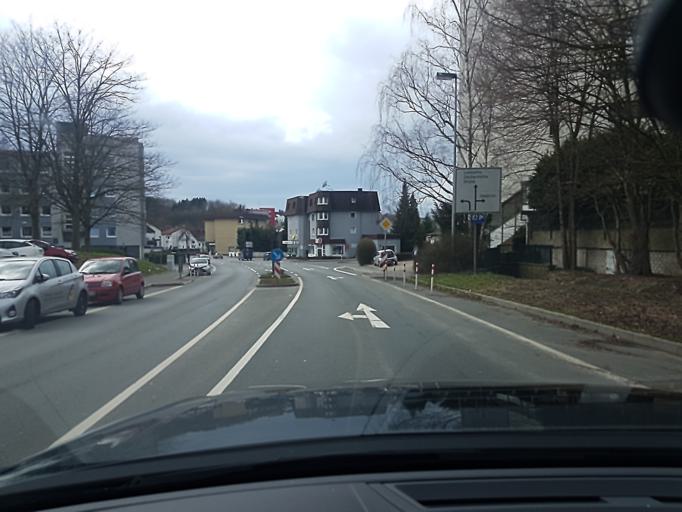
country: DE
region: North Rhine-Westphalia
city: Iserlohn
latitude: 51.3759
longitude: 7.6602
